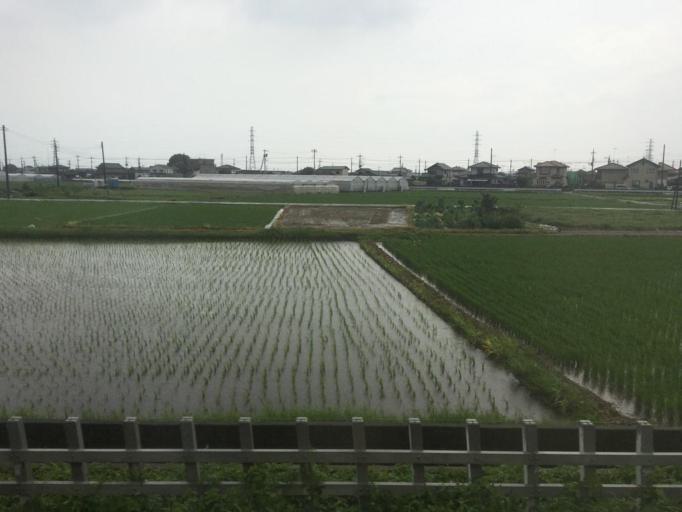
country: JP
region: Tochigi
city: Ashikaga
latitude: 36.2985
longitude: 139.4617
